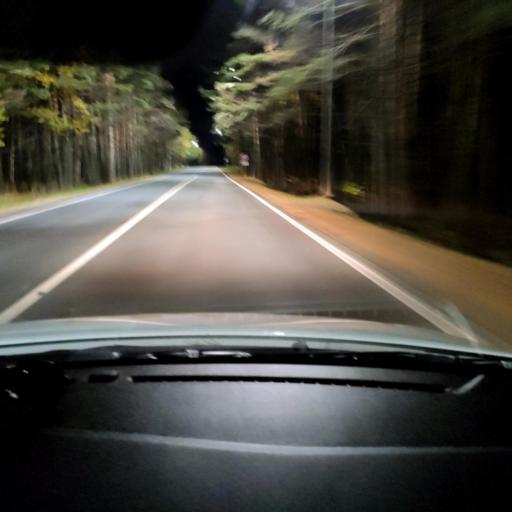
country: RU
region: Tatarstan
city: Verkhniy Uslon
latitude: 55.6348
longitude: 49.0195
